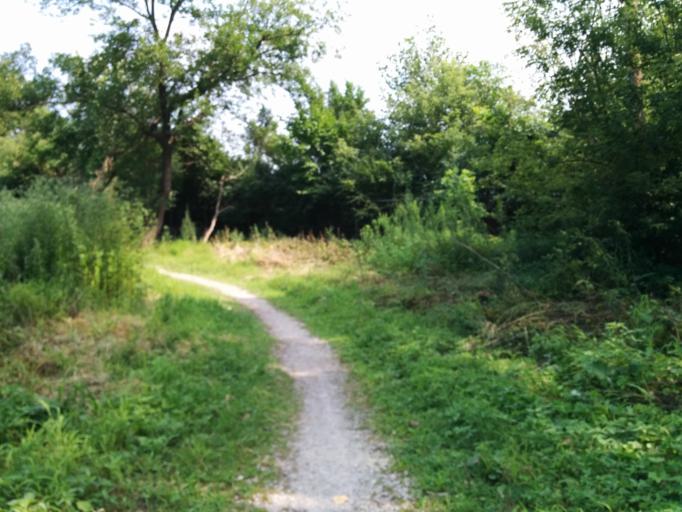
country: US
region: Illinois
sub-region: Cook County
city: Summit
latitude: 41.8034
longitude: -87.8040
